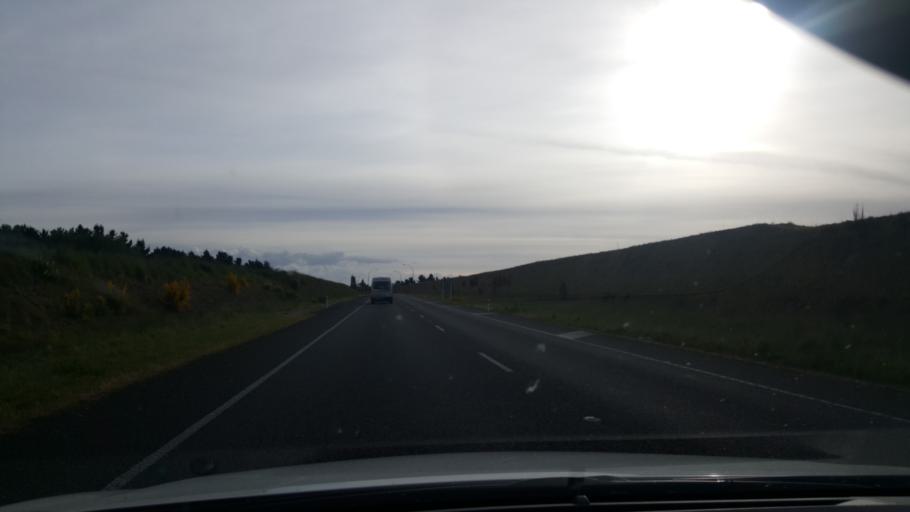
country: NZ
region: Waikato
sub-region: Taupo District
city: Taupo
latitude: -38.7337
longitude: 176.0787
